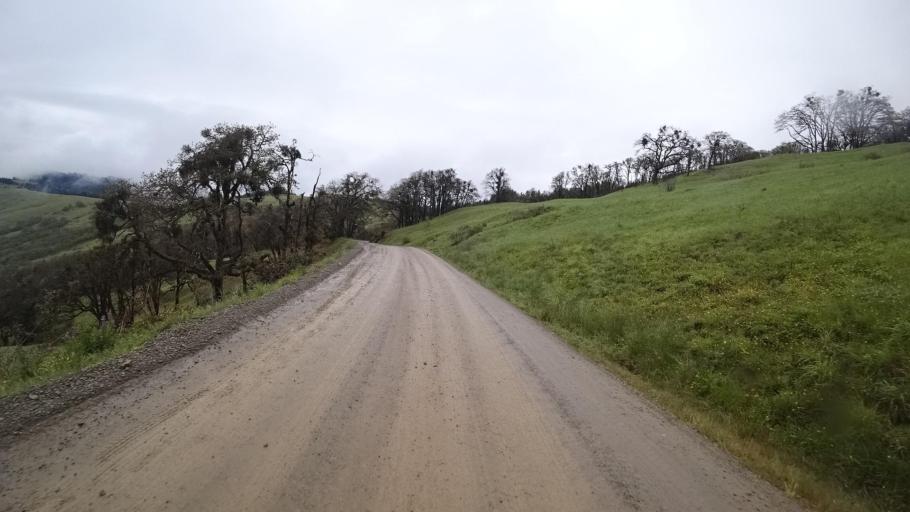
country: US
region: California
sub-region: Humboldt County
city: Westhaven-Moonstone
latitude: 41.1500
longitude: -123.8920
